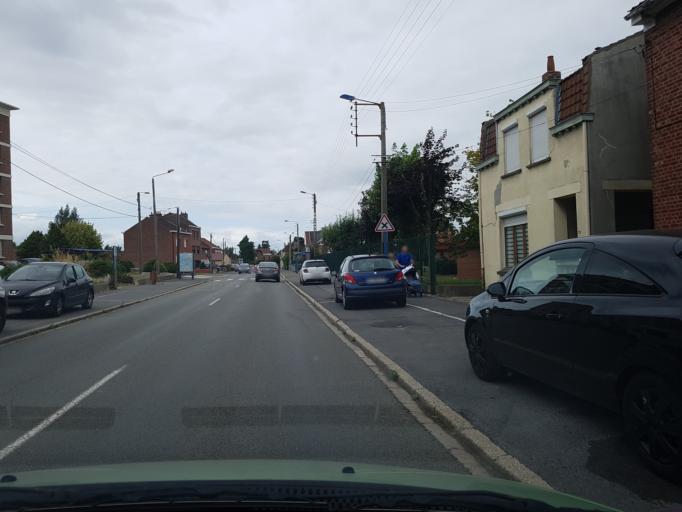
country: FR
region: Nord-Pas-de-Calais
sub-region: Departement du Nord
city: Annoeullin
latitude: 50.5328
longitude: 2.9284
